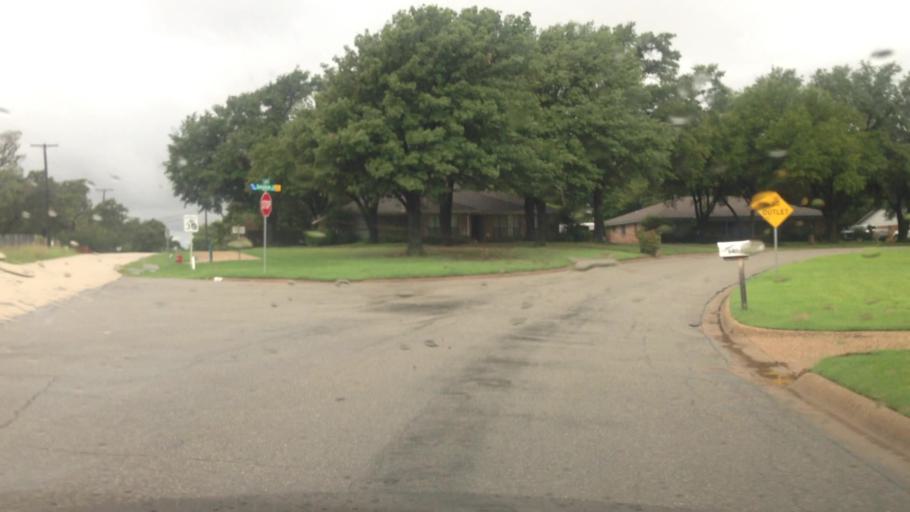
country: US
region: Texas
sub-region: Tarrant County
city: North Richland Hills
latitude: 32.8634
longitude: -97.2010
